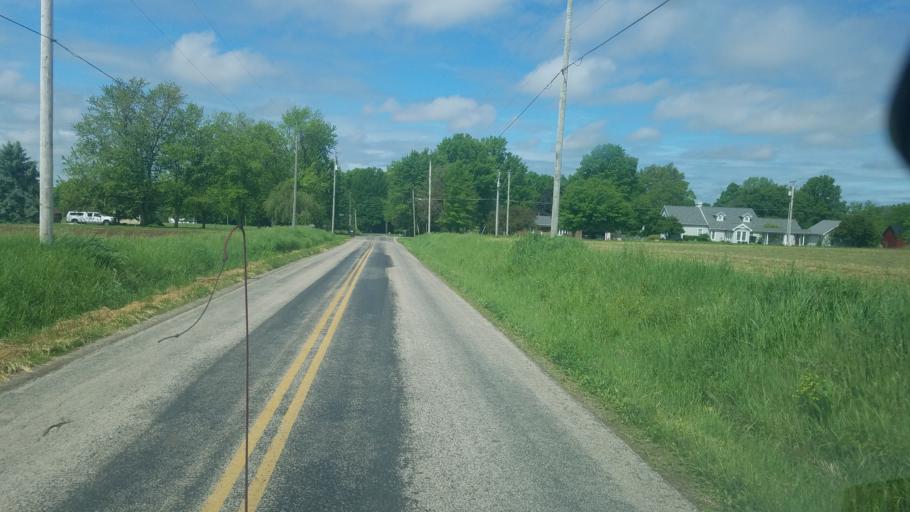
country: US
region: Ohio
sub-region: Wayne County
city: Orrville
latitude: 40.8500
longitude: -81.8119
